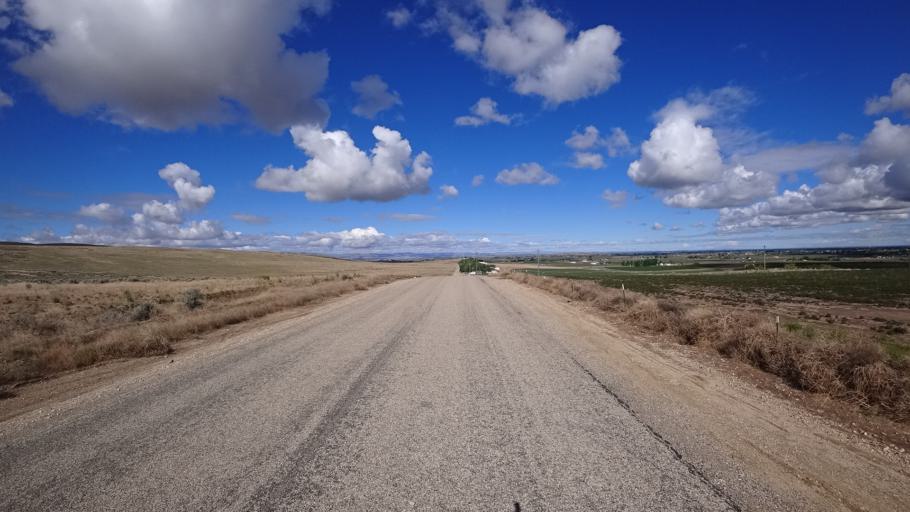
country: US
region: Idaho
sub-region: Ada County
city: Kuna
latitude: 43.4592
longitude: -116.4371
